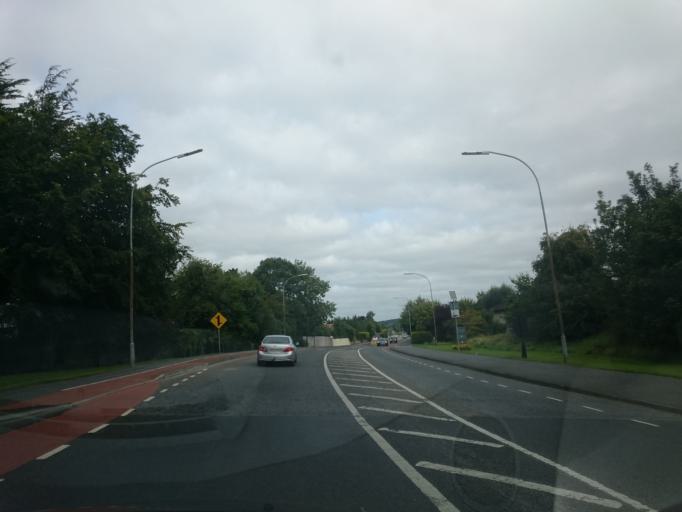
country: IE
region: Leinster
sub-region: Kilkenny
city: Kilkenny
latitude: 52.6717
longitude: -7.2535
